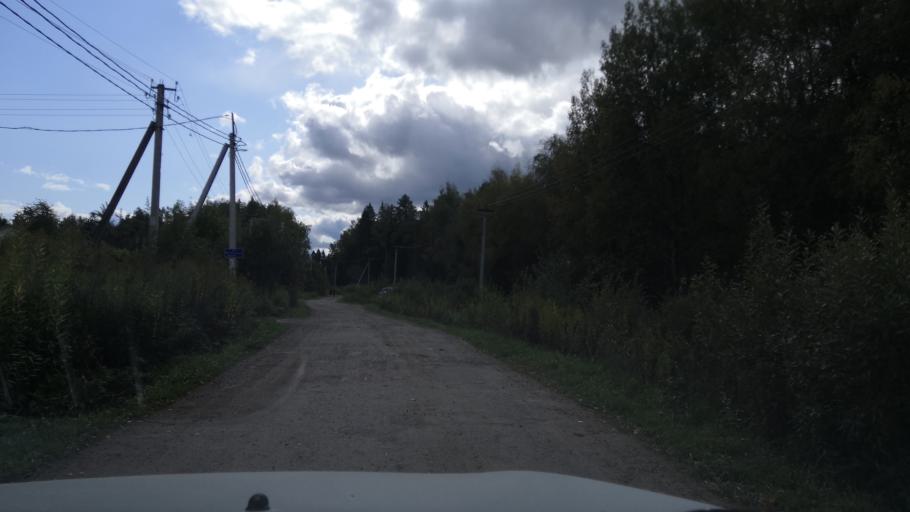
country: RU
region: Moskovskaya
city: Povarovo
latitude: 56.0576
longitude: 37.0202
